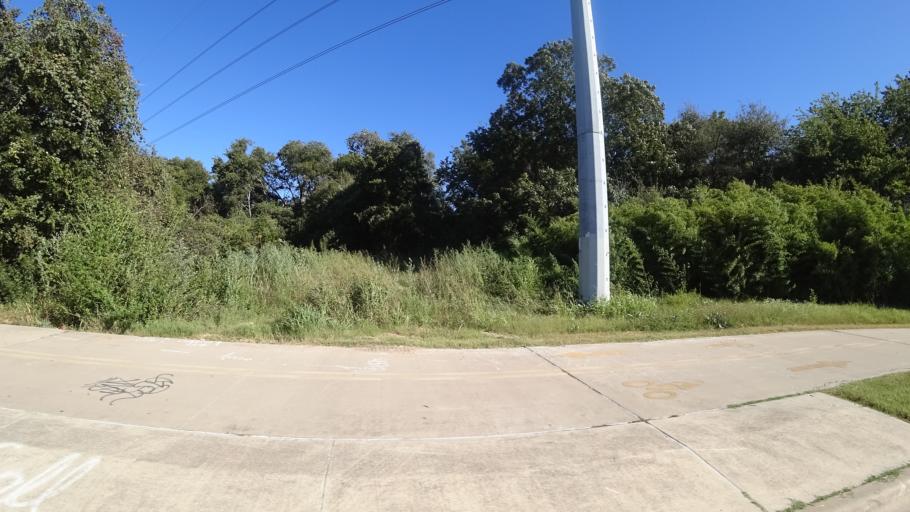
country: US
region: Texas
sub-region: Travis County
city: Austin
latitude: 30.2722
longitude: -97.7638
